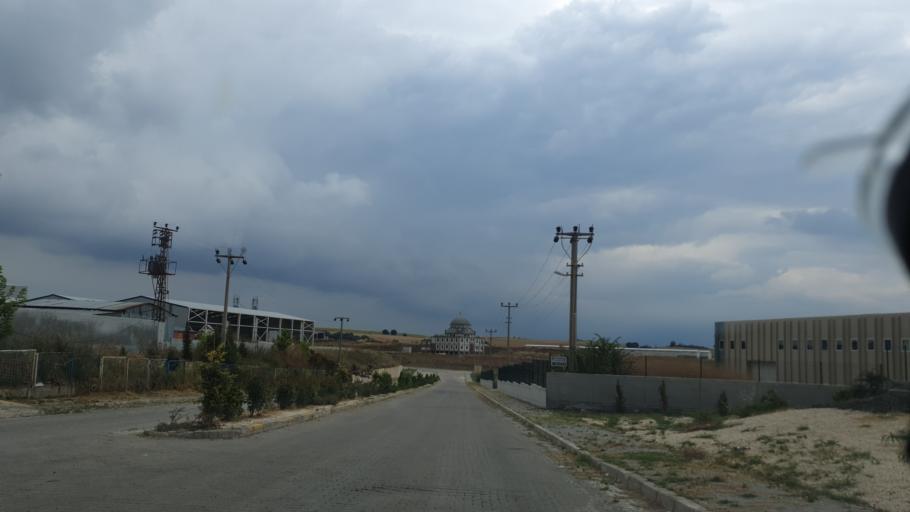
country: TR
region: Tekirdag
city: Hayrabolu
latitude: 41.2237
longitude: 27.0471
